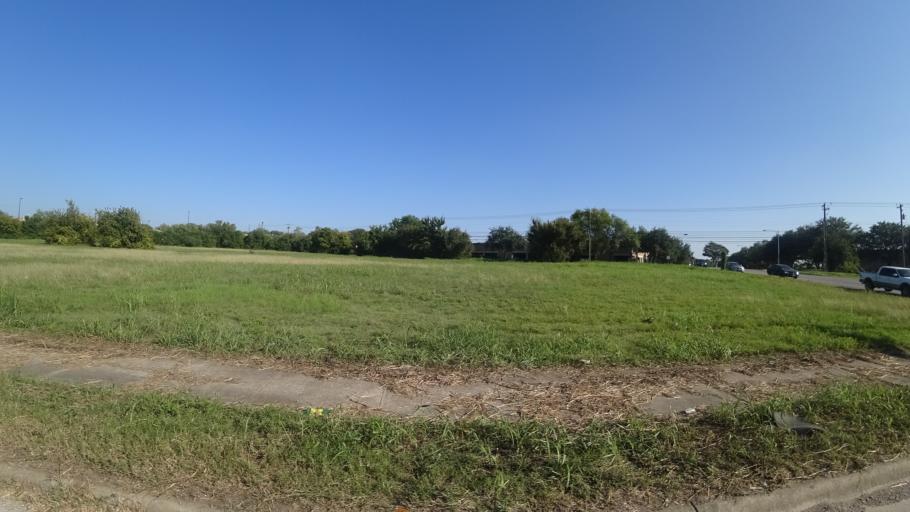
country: US
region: Texas
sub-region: Travis County
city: Austin
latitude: 30.3442
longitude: -97.6781
